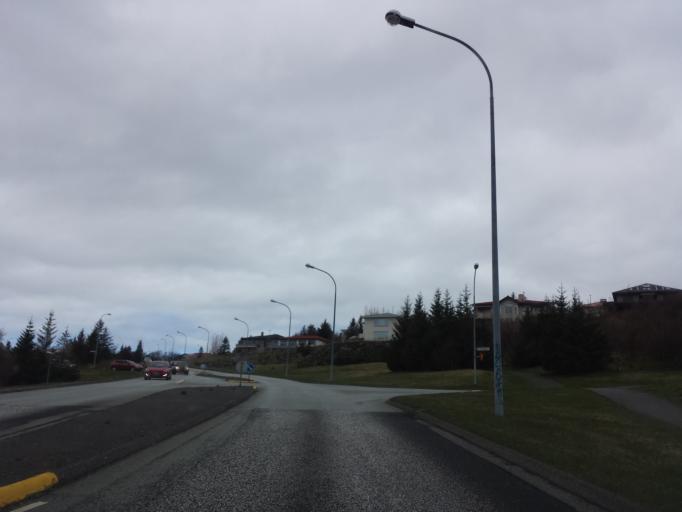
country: IS
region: Capital Region
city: Reykjavik
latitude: 64.1078
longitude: -21.8826
